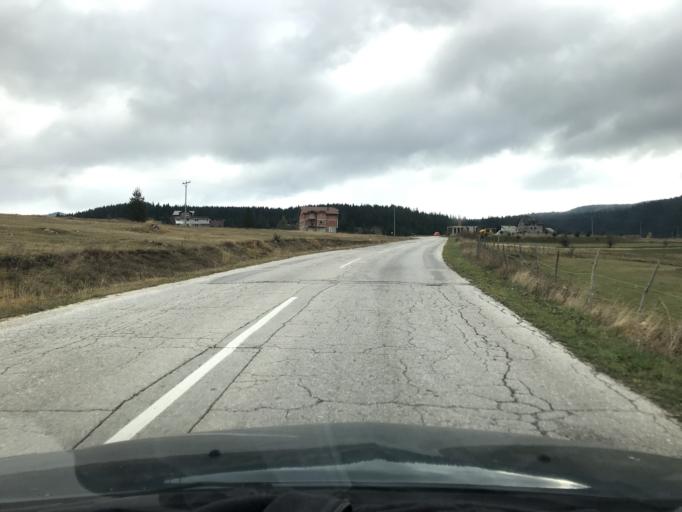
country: BA
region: Federation of Bosnia and Herzegovina
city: Turbe
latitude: 44.3088
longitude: 17.5437
